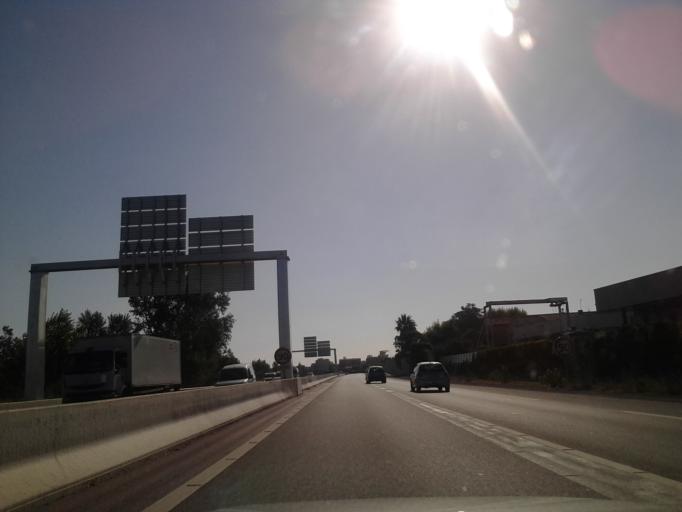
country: FR
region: Languedoc-Roussillon
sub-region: Departement des Pyrenees-Orientales
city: Saint-Esteve
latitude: 42.6982
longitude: 2.8681
